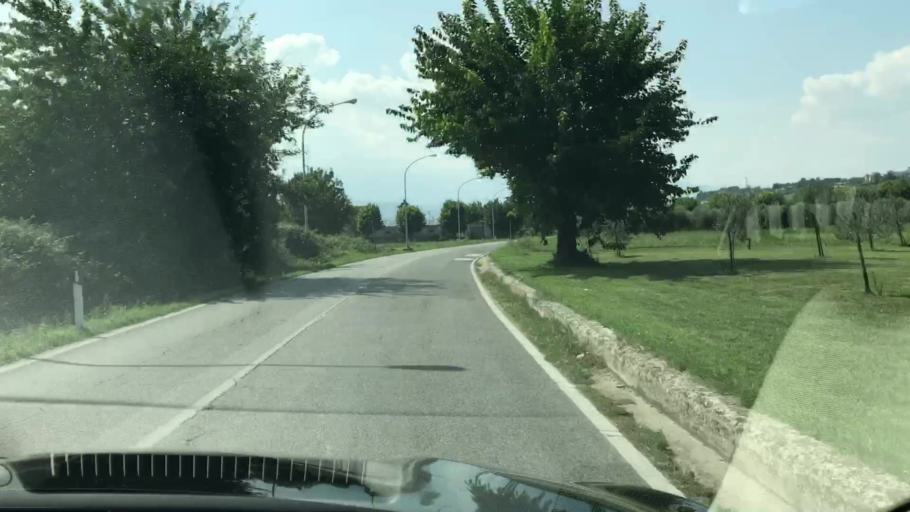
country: IT
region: The Marches
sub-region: Provincia di Ascoli Piceno
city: Monsampolo del Tronto
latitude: 42.8801
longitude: 13.7877
